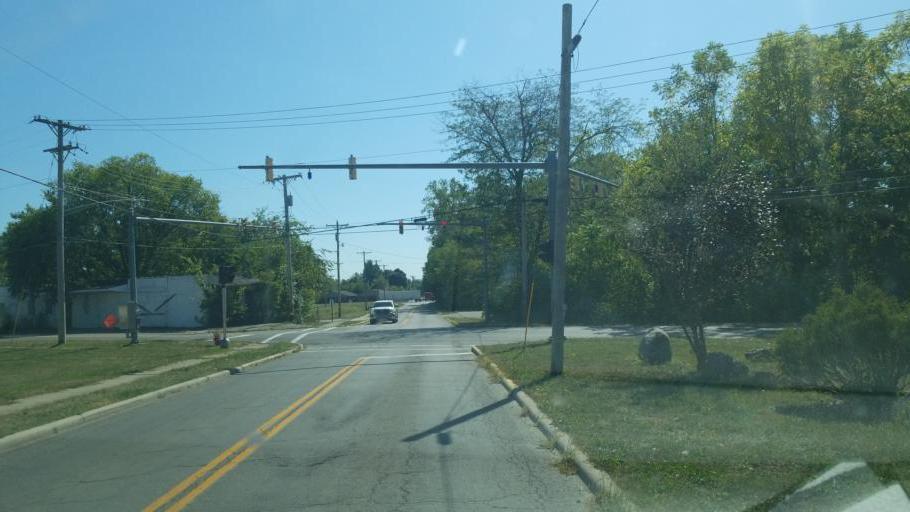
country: US
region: Ohio
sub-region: Logan County
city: Bellefontaine
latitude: 40.3660
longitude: -83.7728
